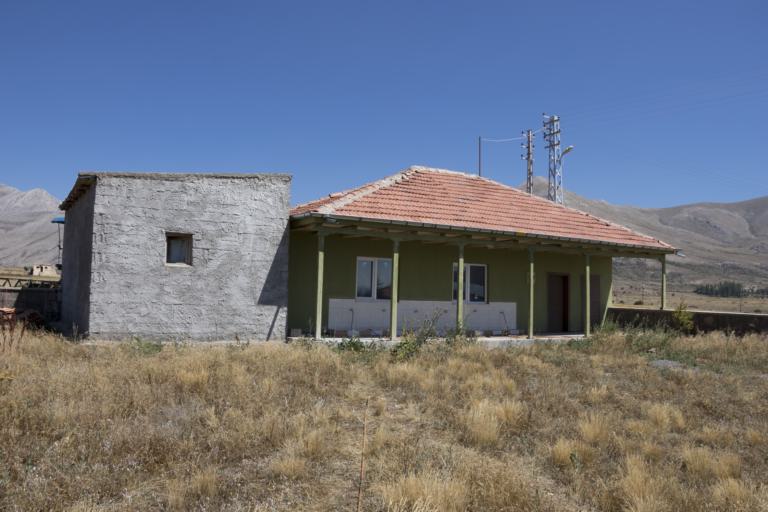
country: TR
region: Kayseri
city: Toklar
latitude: 38.4074
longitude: 36.0847
